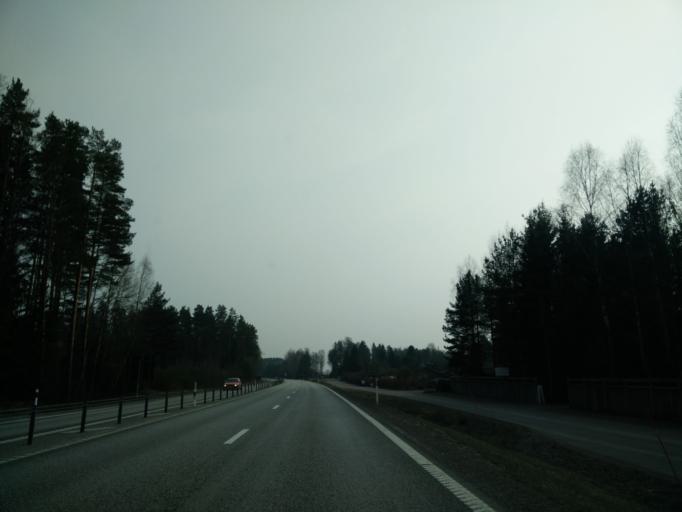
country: SE
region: Vaermland
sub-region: Forshaga Kommun
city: Forshaga
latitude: 59.4796
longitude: 13.4110
